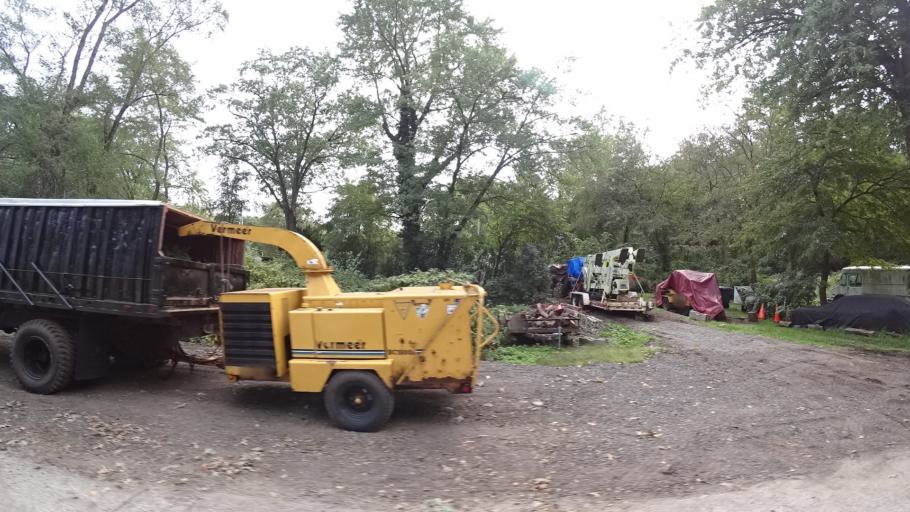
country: US
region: Indiana
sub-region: LaPorte County
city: Long Beach
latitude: 41.7293
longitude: -86.8560
